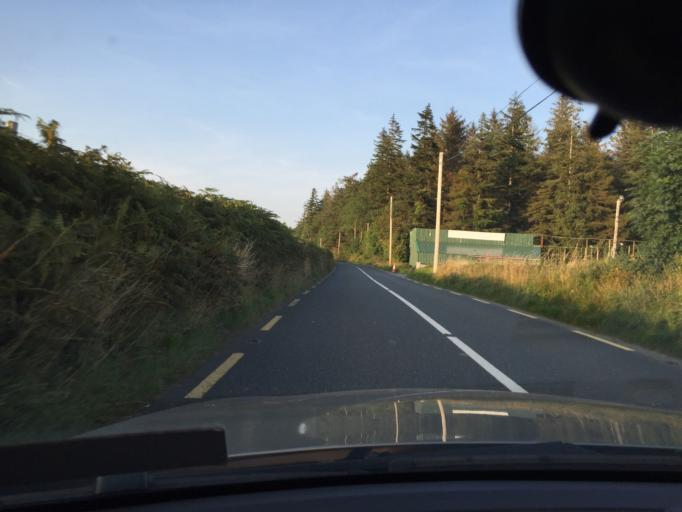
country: IE
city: Newtownmountkennedy
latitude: 53.0746
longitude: -6.2169
